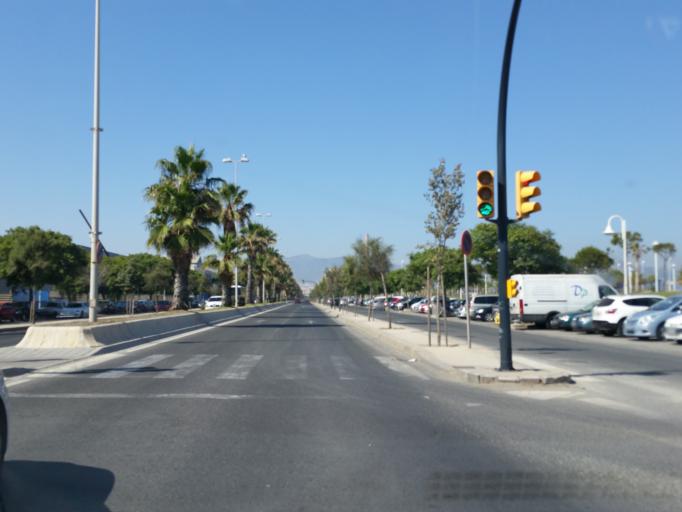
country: ES
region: Andalusia
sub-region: Provincia de Malaga
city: Malaga
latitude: 36.6844
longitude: -4.4462
